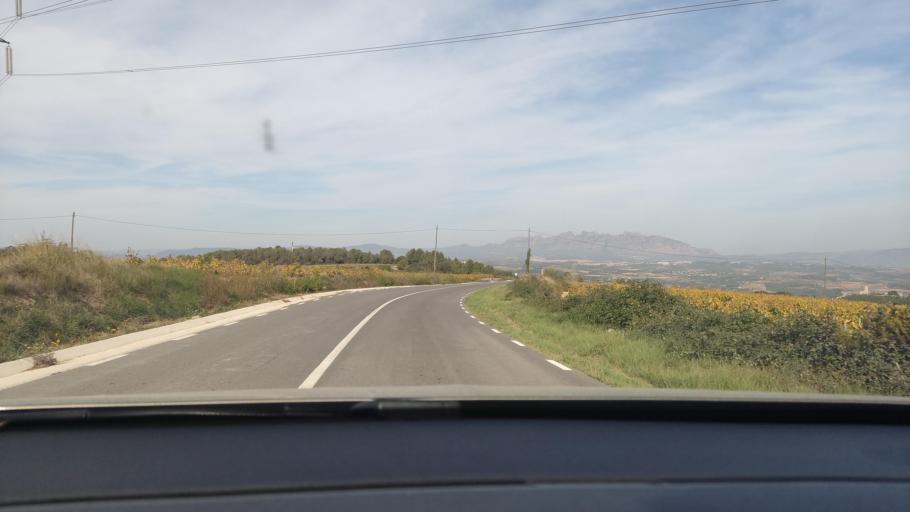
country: ES
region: Catalonia
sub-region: Provincia de Barcelona
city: Subirats
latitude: 41.4024
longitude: 1.8105
